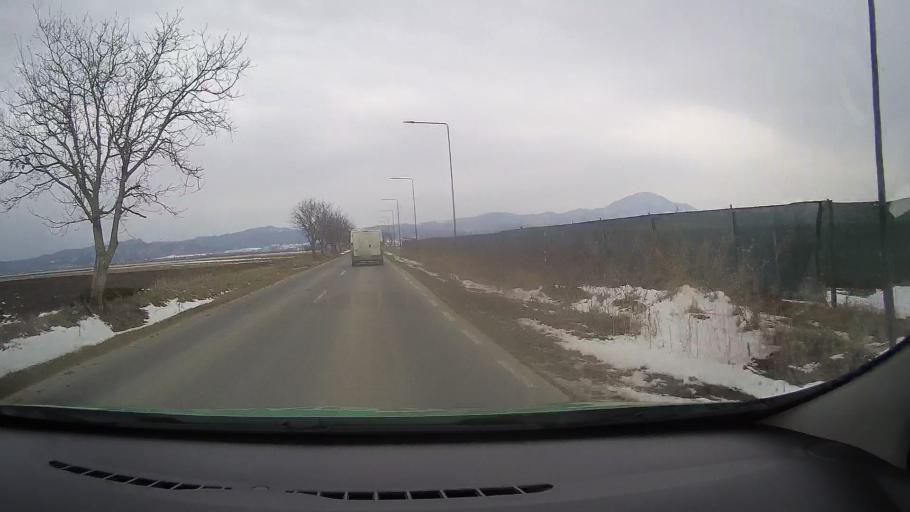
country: RO
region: Brasov
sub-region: Comuna Cristian
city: Cristian
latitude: 45.6315
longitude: 25.4609
